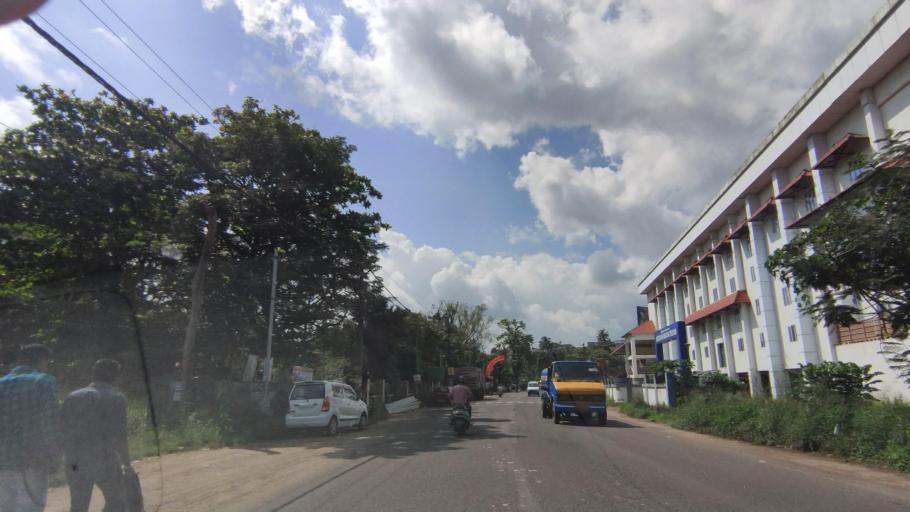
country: IN
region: Kerala
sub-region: Kottayam
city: Kottayam
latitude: 9.5935
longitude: 76.5277
